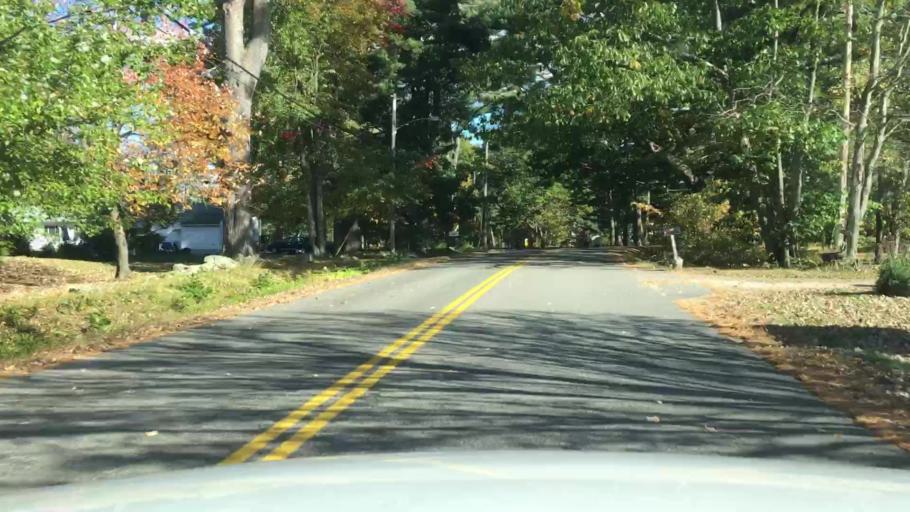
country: US
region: Maine
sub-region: York County
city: Wells Beach Station
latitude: 43.3350
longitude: -70.6271
